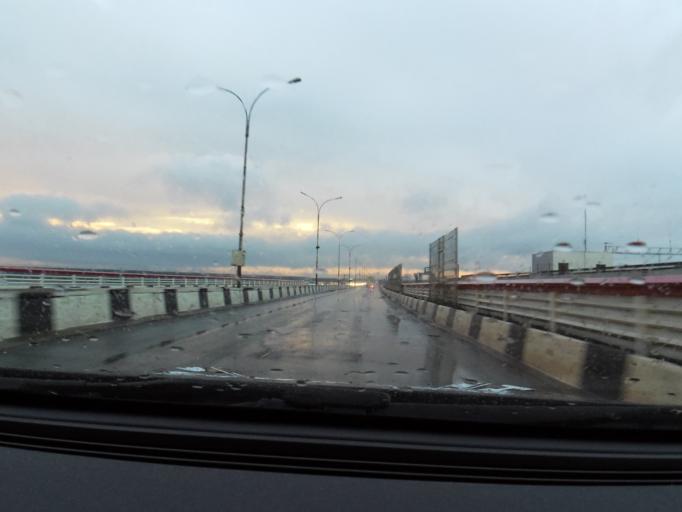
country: RU
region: Tatarstan
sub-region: Tukayevskiy Rayon
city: Naberezhnyye Chelny
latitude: 55.6957
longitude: 52.2801
